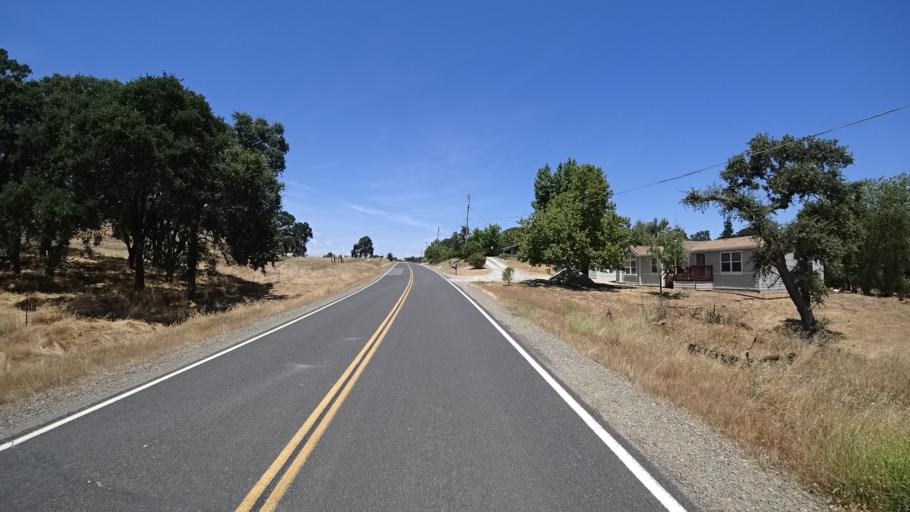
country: US
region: California
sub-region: Calaveras County
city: Rancho Calaveras
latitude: 38.1017
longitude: -120.8789
